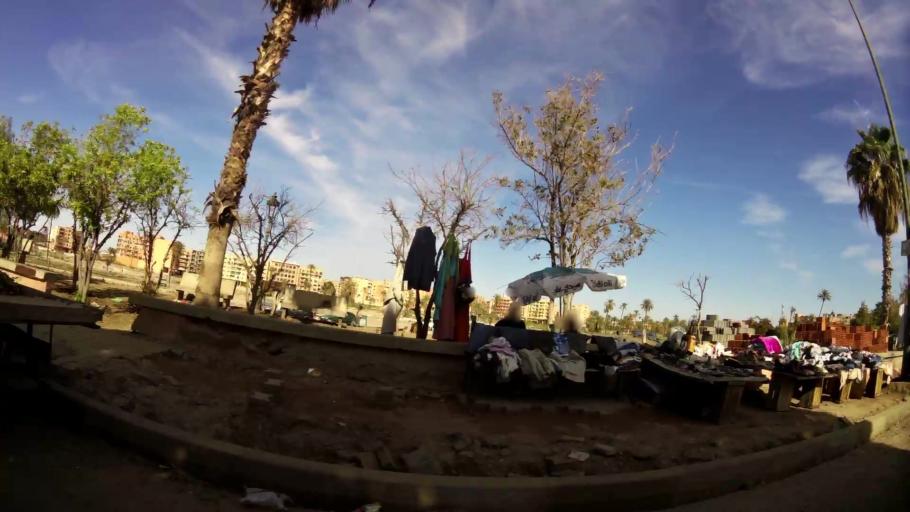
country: MA
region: Marrakech-Tensift-Al Haouz
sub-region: Marrakech
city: Marrakesh
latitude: 31.6520
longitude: -8.0246
